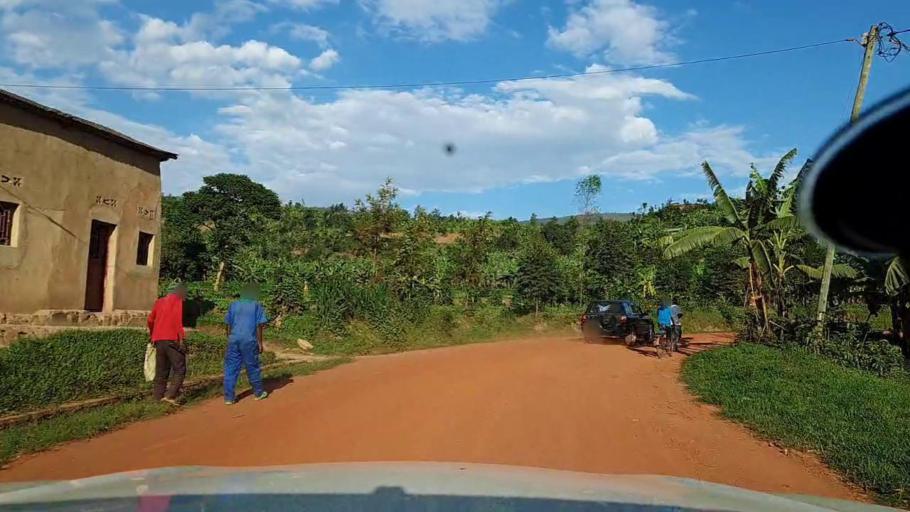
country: RW
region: Kigali
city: Kigali
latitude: -1.8636
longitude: 29.9227
